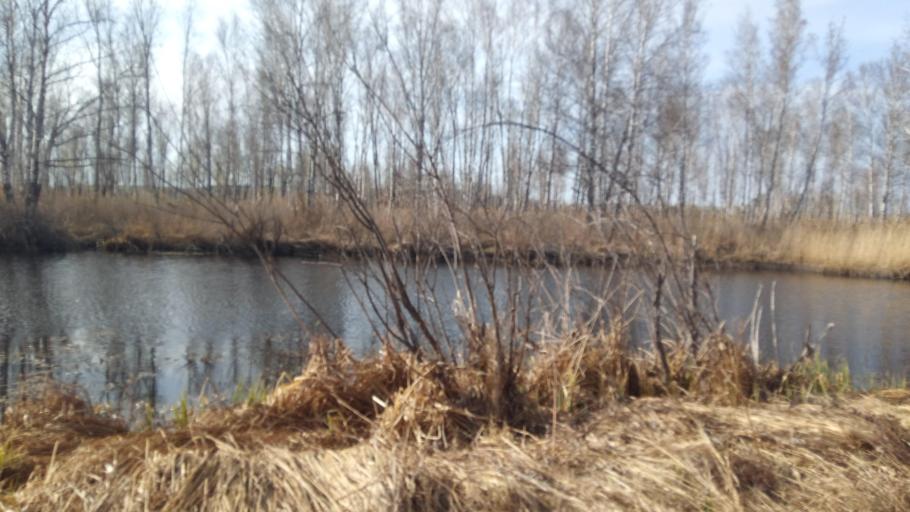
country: RU
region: Chelyabinsk
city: Poletayevo
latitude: 55.0317
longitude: 61.0745
